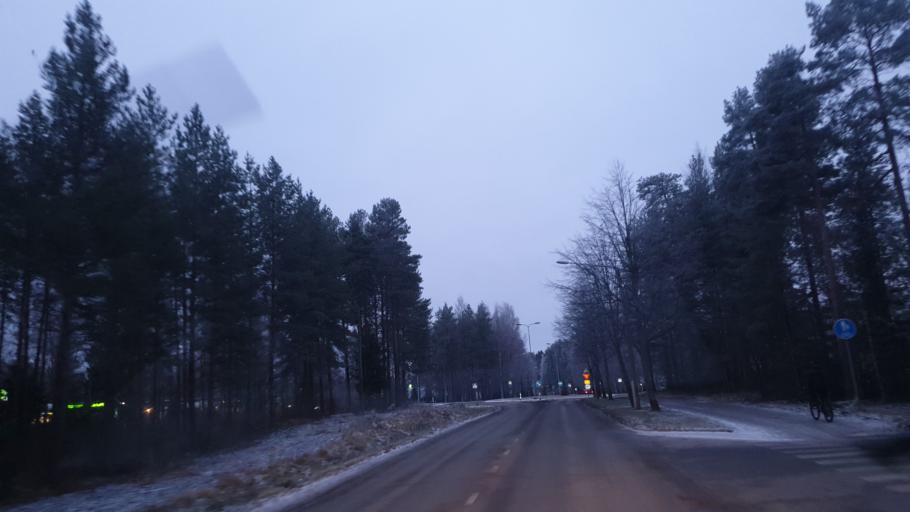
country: FI
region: Southern Ostrobothnia
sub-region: Seinaejoki
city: Seinaejoki
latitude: 62.7726
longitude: 22.8768
